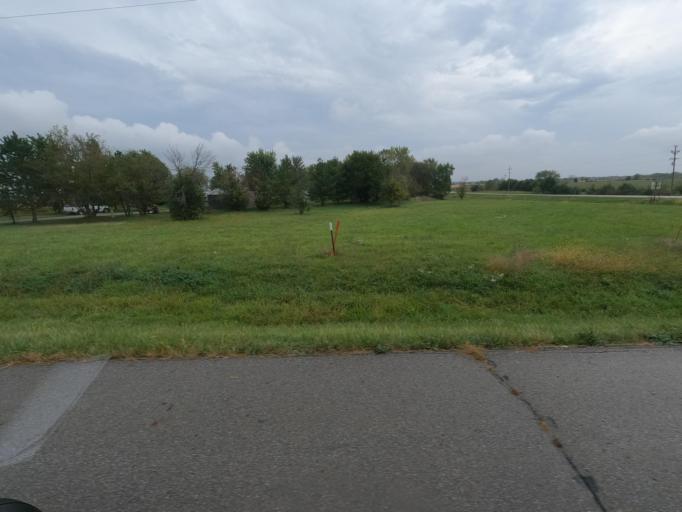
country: US
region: Iowa
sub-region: Van Buren County
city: Keosauqua
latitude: 40.8087
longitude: -91.9293
